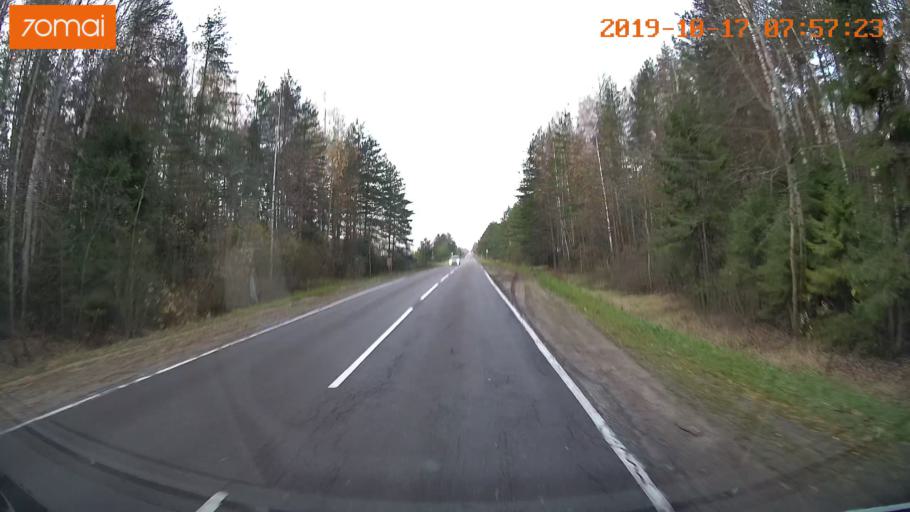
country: RU
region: Vladimir
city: Bavleny
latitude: 56.4122
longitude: 39.5773
